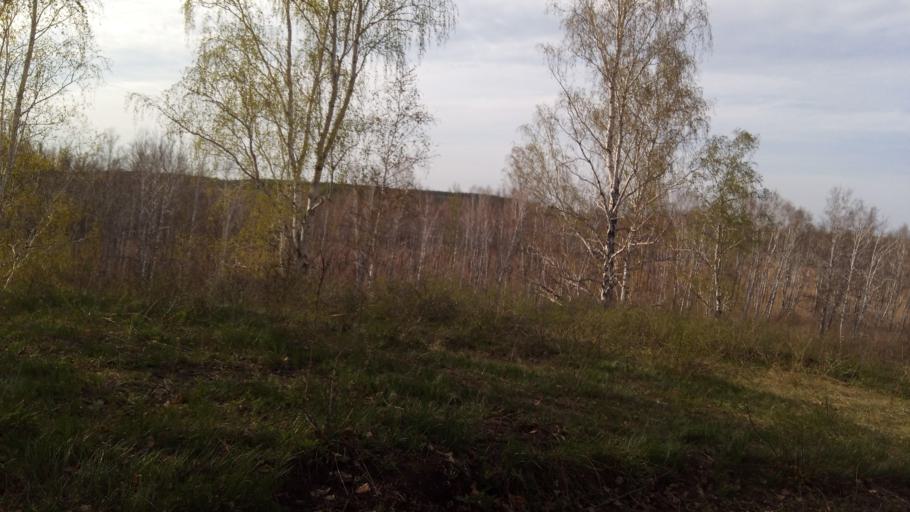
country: RU
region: Chelyabinsk
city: Poletayevo
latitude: 55.0312
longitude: 61.0743
